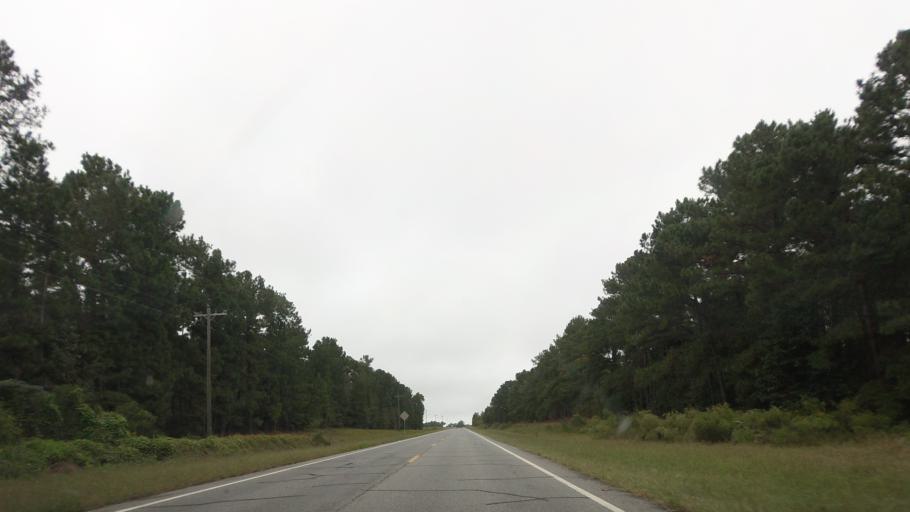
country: US
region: Georgia
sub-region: Irwin County
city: Ocilla
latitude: 31.5020
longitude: -83.2388
